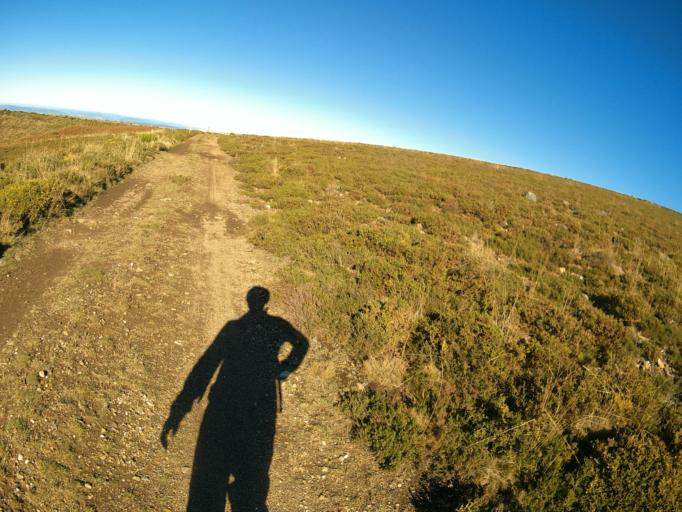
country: PT
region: Vila Real
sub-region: Mesao Frio
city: Mesao Frio
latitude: 41.2324
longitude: -7.9152
